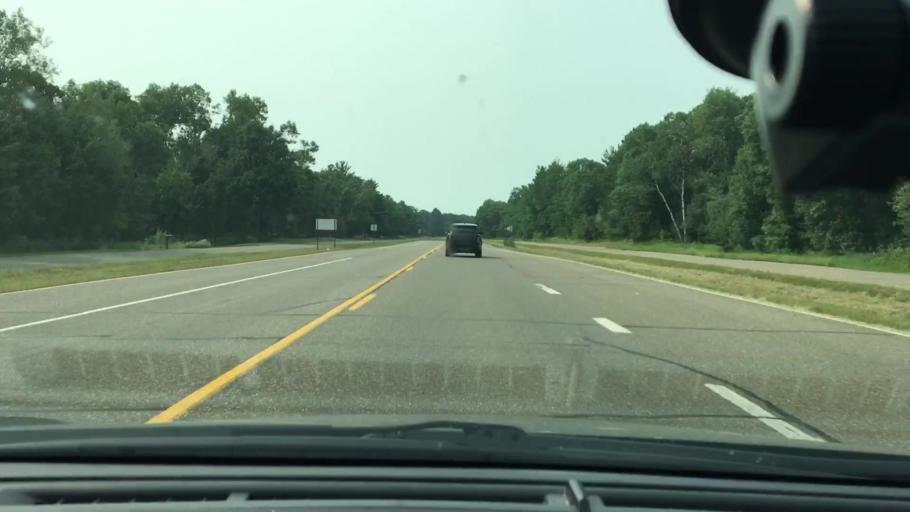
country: US
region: Minnesota
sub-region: Crow Wing County
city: Breezy Point
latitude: 46.4999
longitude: -94.1437
